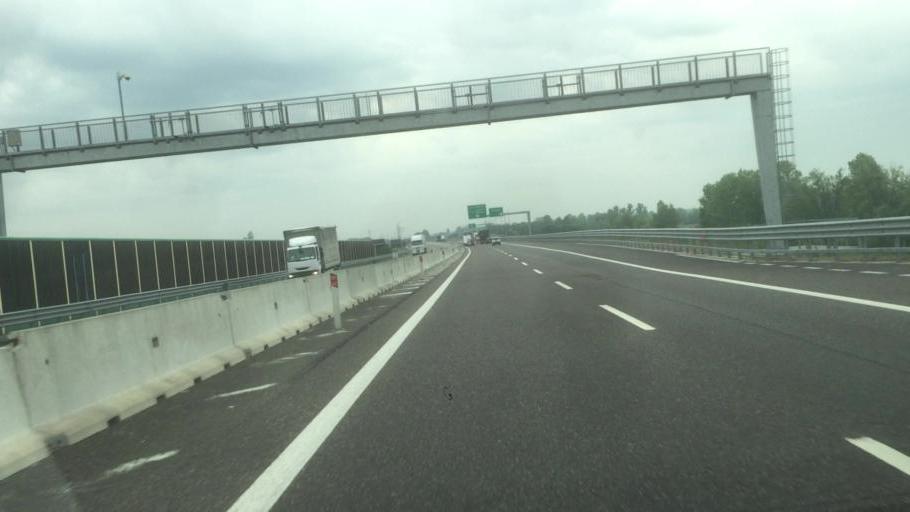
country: IT
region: Lombardy
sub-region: Provincia di Brescia
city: Capriano del Colle
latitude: 45.4784
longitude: 10.1491
